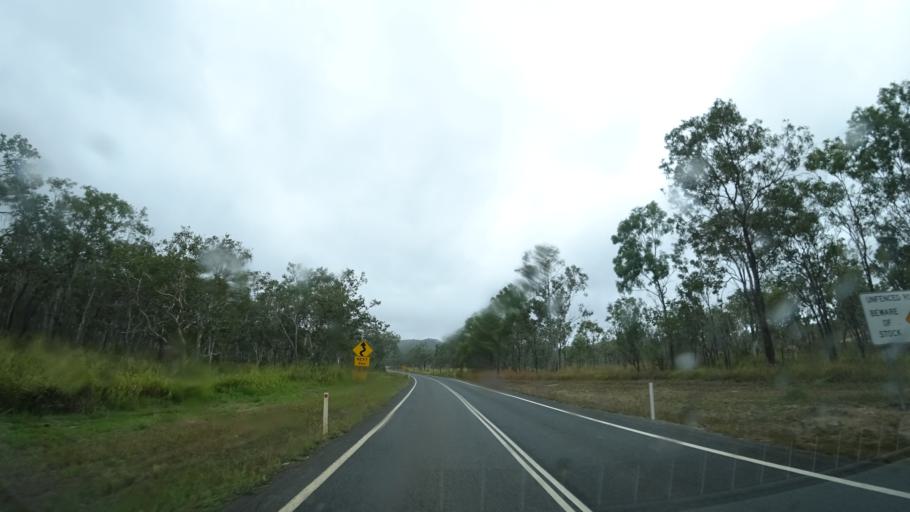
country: AU
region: Queensland
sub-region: Cairns
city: Port Douglas
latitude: -16.6941
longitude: 145.3398
